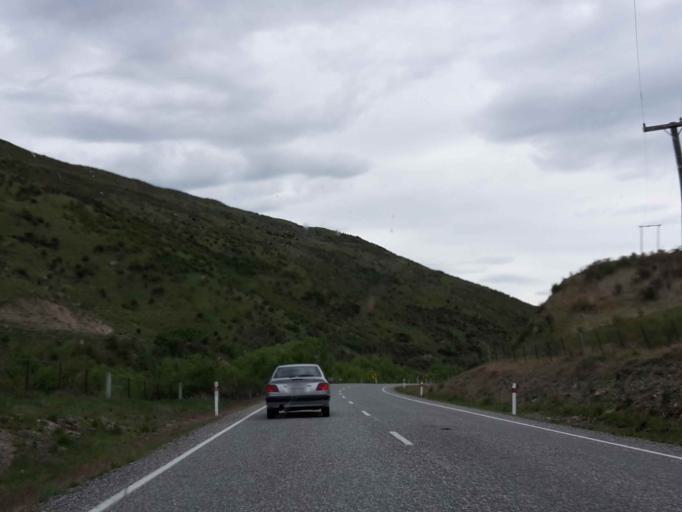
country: NZ
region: Otago
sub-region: Queenstown-Lakes District
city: Wanaka
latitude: -44.7303
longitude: 169.5074
